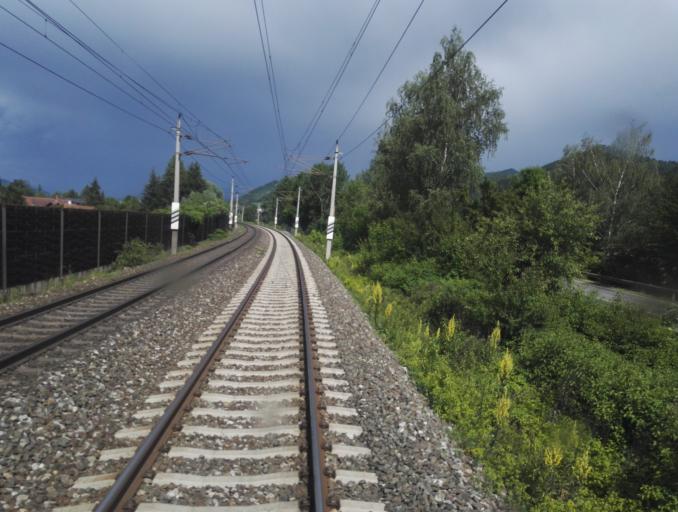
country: AT
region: Styria
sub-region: Politischer Bezirk Bruck-Muerzzuschlag
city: Kapfenberg
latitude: 47.4509
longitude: 15.3184
